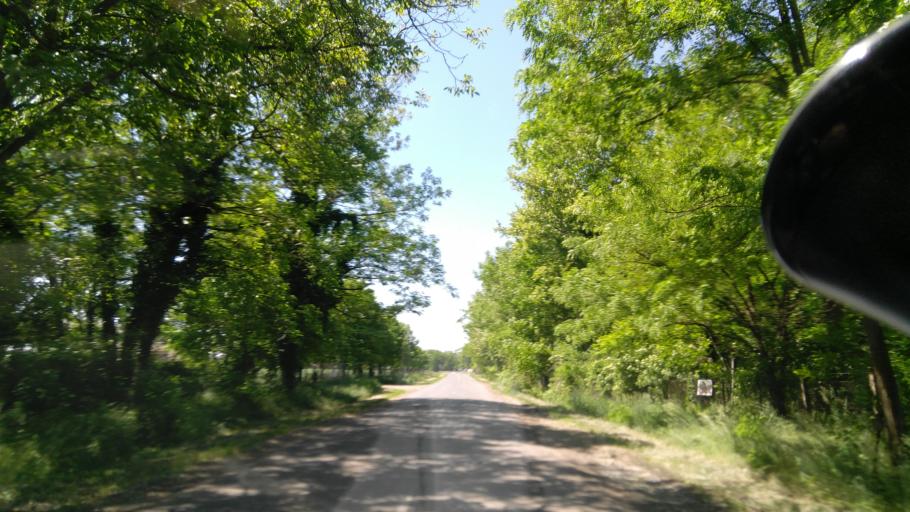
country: HU
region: Bekes
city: Kunagota
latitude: 46.4318
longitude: 21.0622
